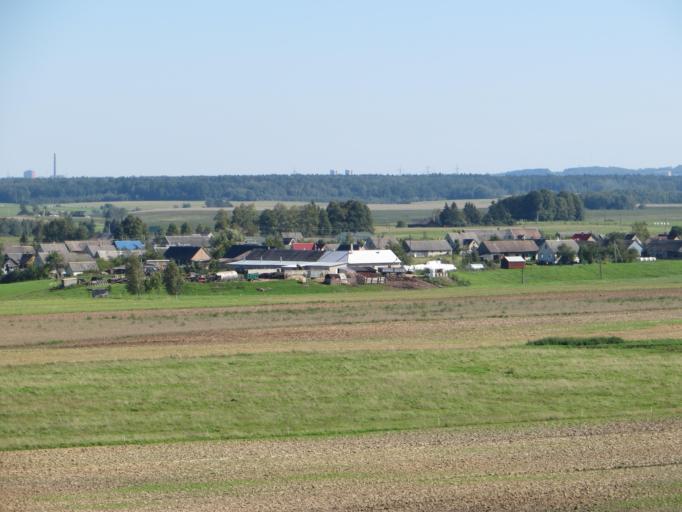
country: LT
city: Prienai
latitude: 54.4821
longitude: 23.8643
